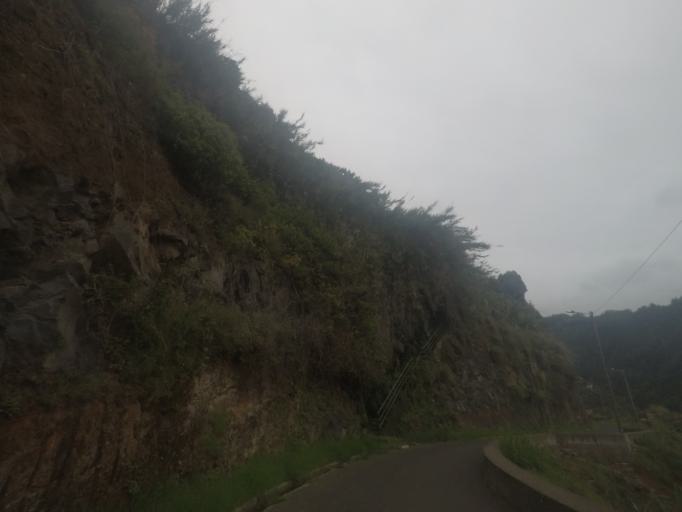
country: PT
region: Madeira
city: Camara de Lobos
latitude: 32.6636
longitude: -16.9620
